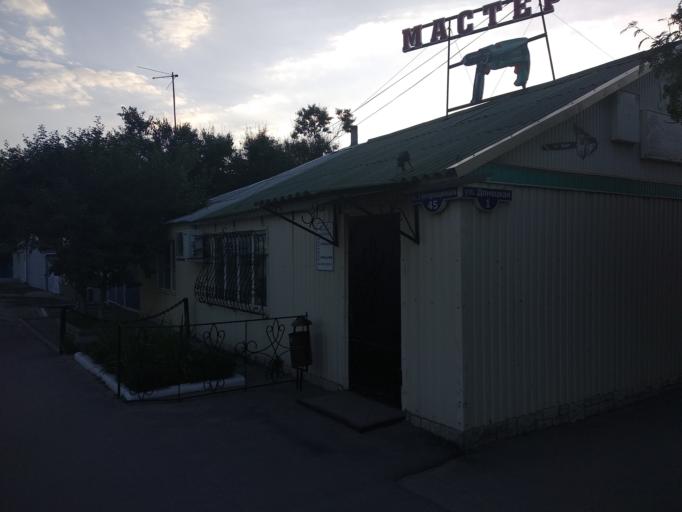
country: RU
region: Rostov
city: Millerovo
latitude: 48.9255
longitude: 40.4051
